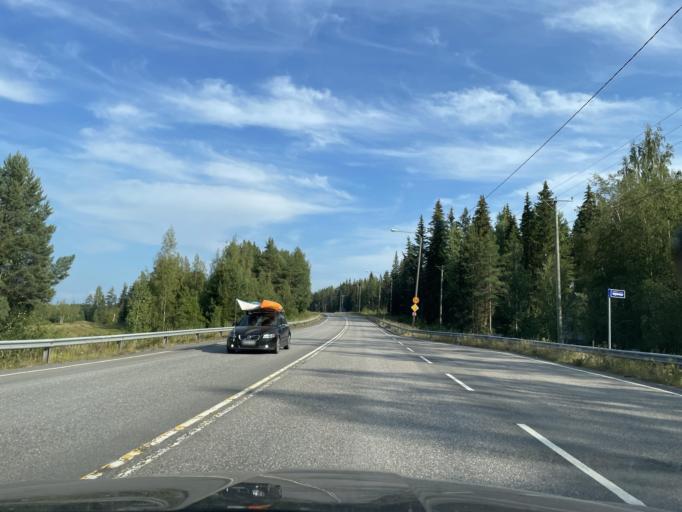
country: FI
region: Central Finland
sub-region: Jaemsae
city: Jaemsae
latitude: 61.8039
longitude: 25.1871
